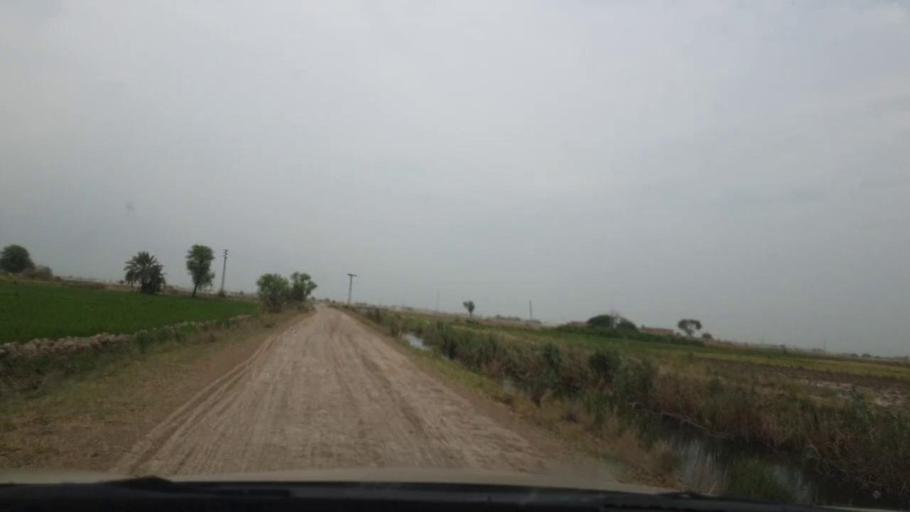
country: PK
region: Sindh
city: Ratodero
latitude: 27.7737
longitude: 68.2772
